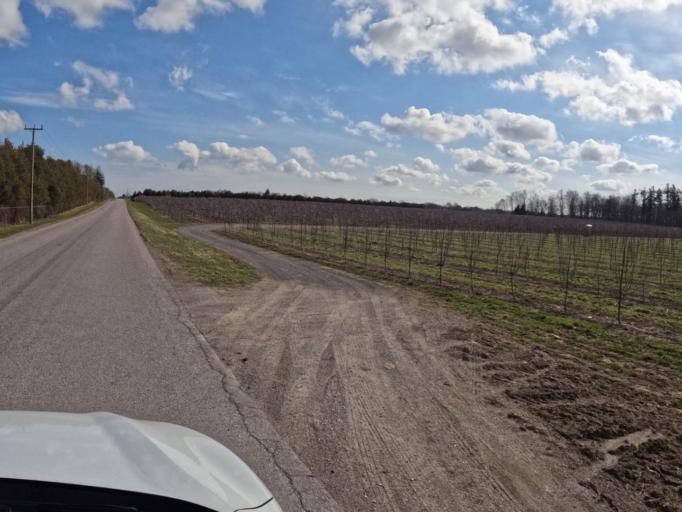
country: CA
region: Ontario
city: Norfolk County
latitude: 42.8595
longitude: -80.2736
